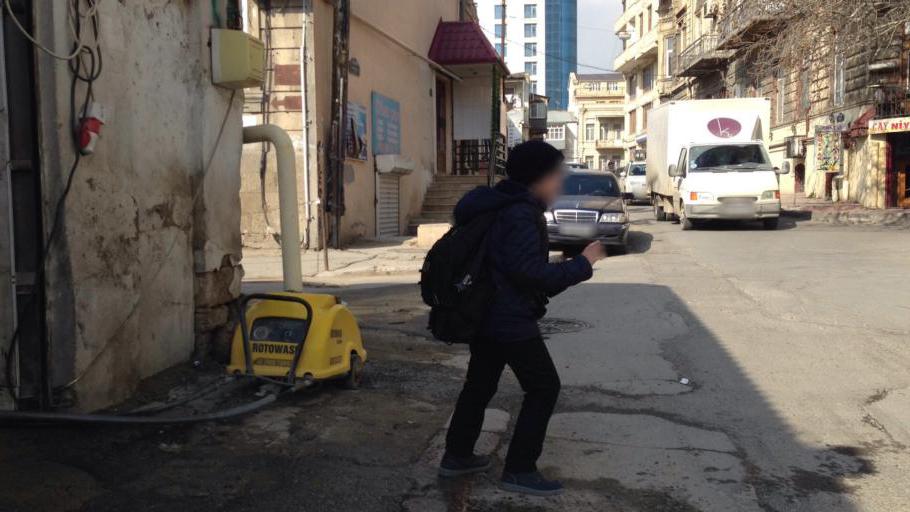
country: AZ
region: Baki
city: Badamdar
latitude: 40.3740
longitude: 49.8382
